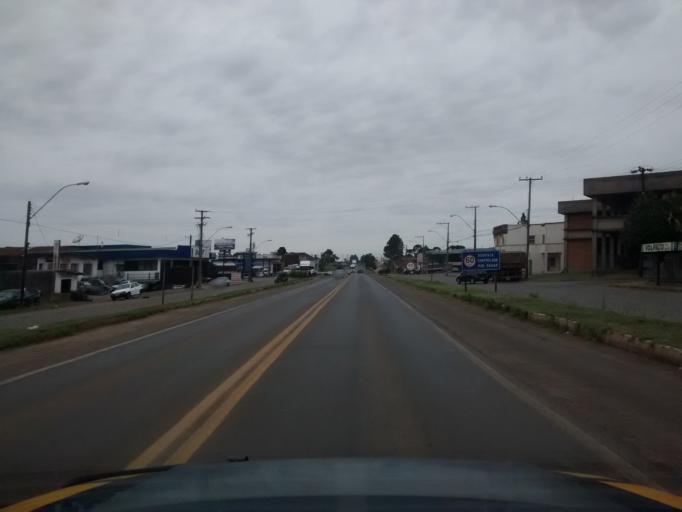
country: BR
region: Rio Grande do Sul
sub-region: Vacaria
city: Vacaria
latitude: -28.5081
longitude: -50.9281
